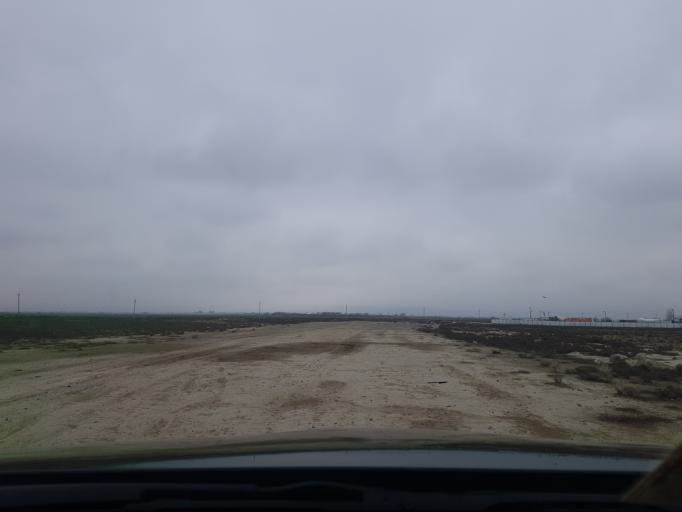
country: TM
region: Ahal
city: Abadan
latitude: 38.1402
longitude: 57.9770
